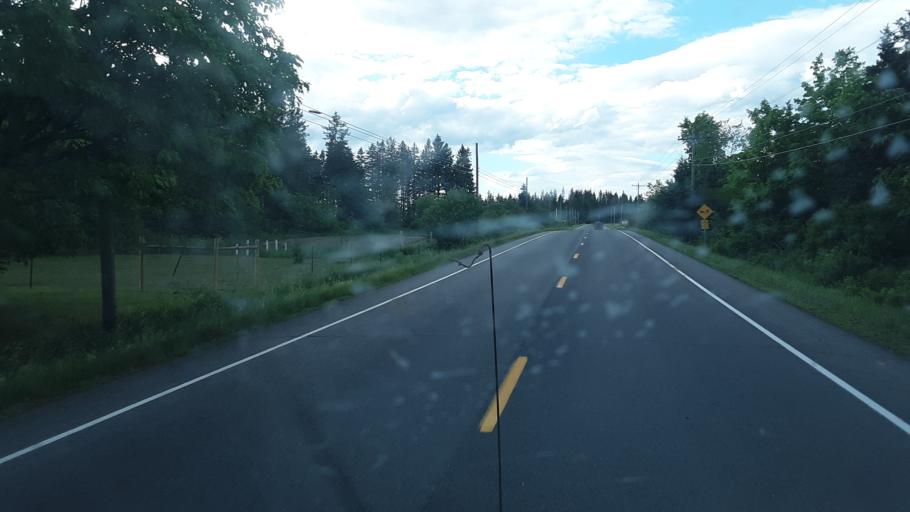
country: US
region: Maine
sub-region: Penobscot County
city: Patten
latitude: 45.9410
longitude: -68.4515
